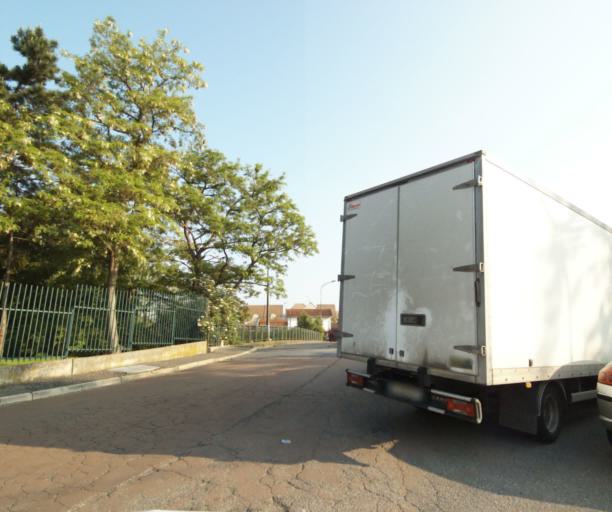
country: FR
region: Ile-de-France
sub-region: Departement du Val-d'Oise
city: Argenteuil
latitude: 48.9473
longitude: 2.2668
